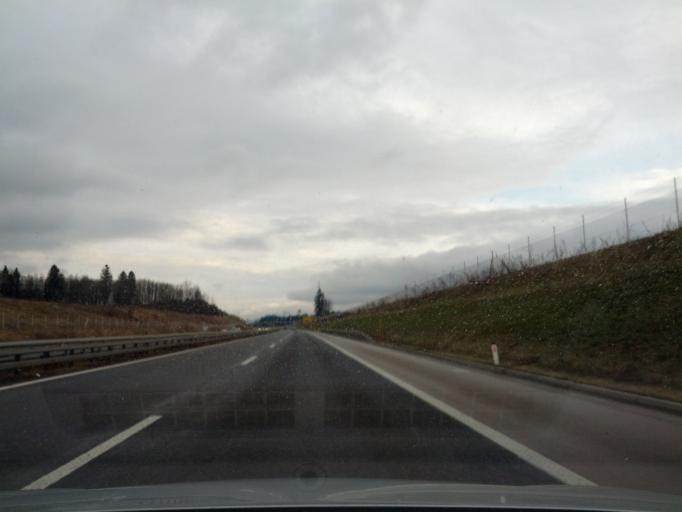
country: SI
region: Radovljica
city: Radovljica
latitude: 46.3466
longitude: 14.1820
